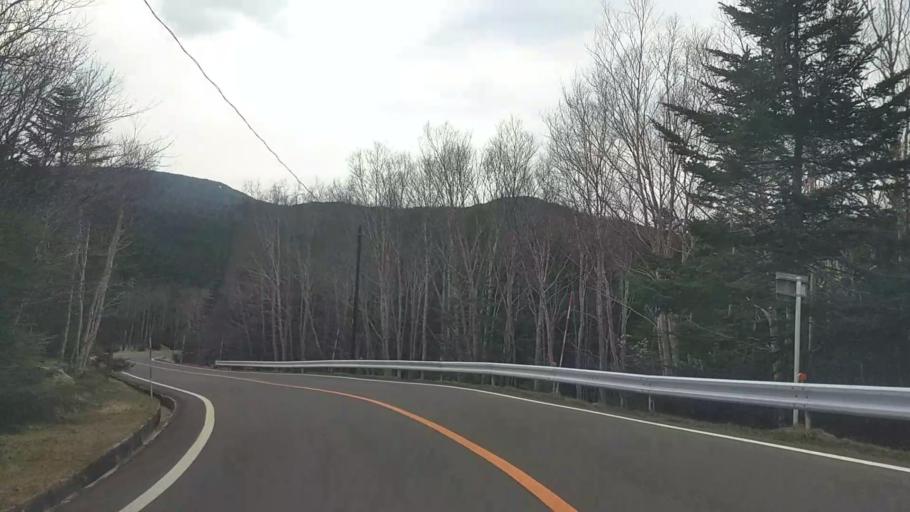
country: JP
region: Nagano
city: Saku
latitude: 36.0593
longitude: 138.3602
